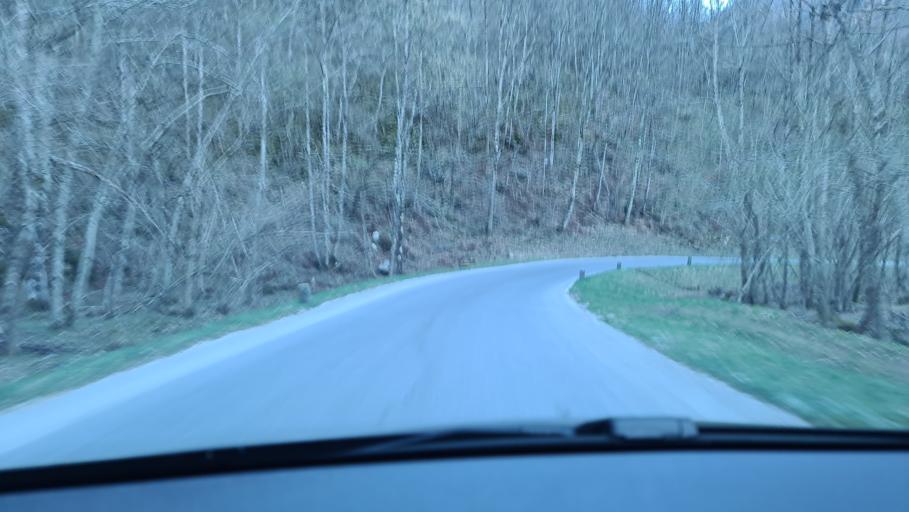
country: CH
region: Ticino
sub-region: Vallemaggia District
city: Cevio
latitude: 46.3767
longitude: 8.5475
